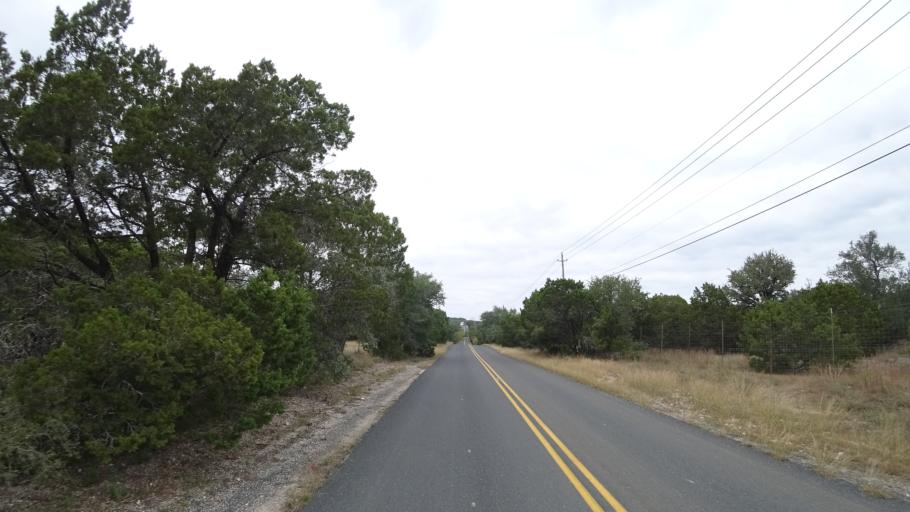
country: US
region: Texas
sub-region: Travis County
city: Lakeway
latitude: 30.3517
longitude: -97.9458
